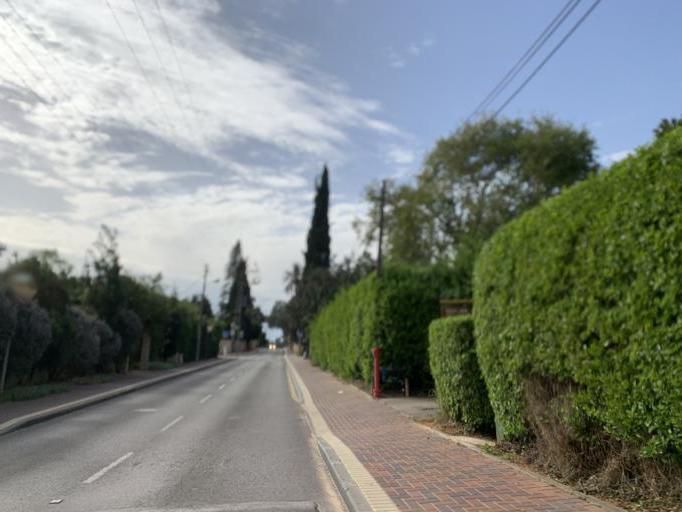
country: IL
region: Central District
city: Hod HaSharon
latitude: 32.1537
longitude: 34.9029
